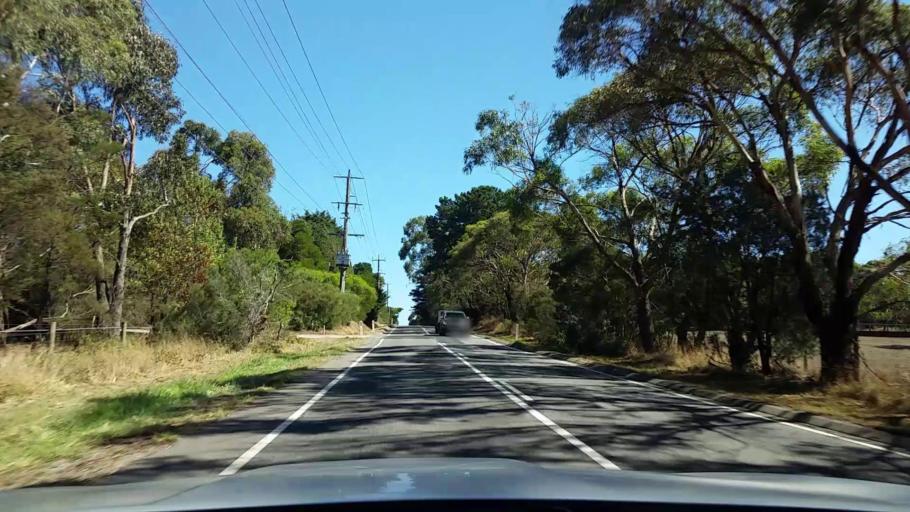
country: AU
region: Victoria
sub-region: Mornington Peninsula
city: Hastings
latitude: -38.2846
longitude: 145.1579
